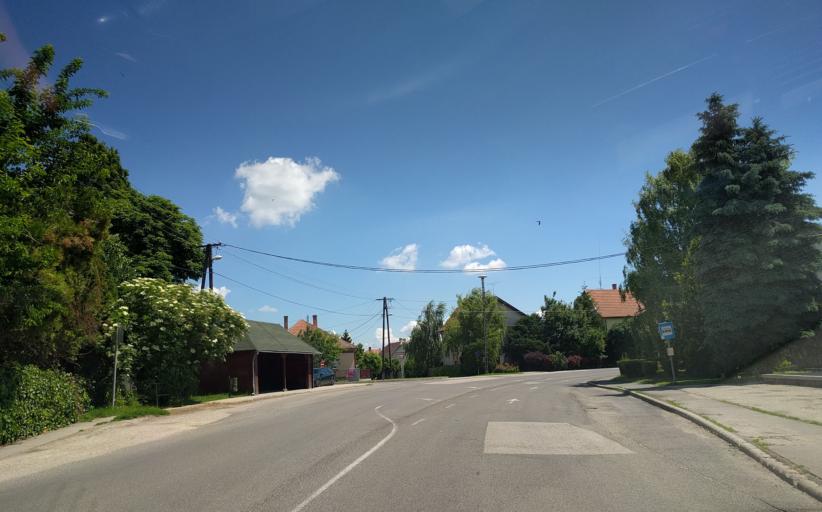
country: HU
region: Jasz-Nagykun-Szolnok
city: Toszeg
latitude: 47.1010
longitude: 20.1474
